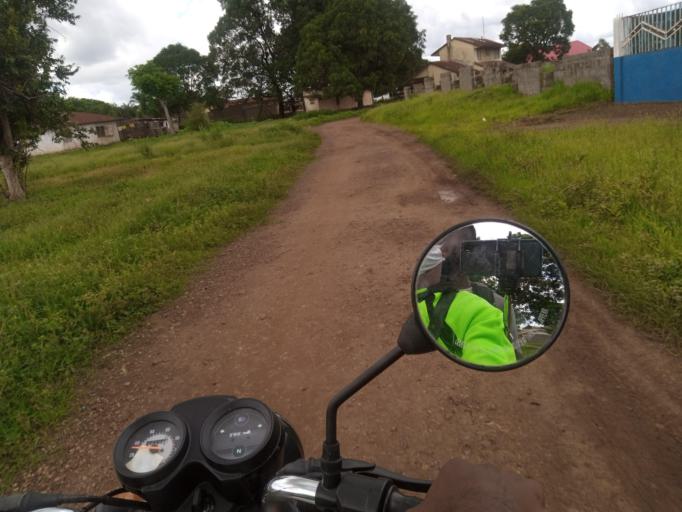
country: SL
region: Northern Province
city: Port Loko
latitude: 8.7658
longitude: -12.7773
